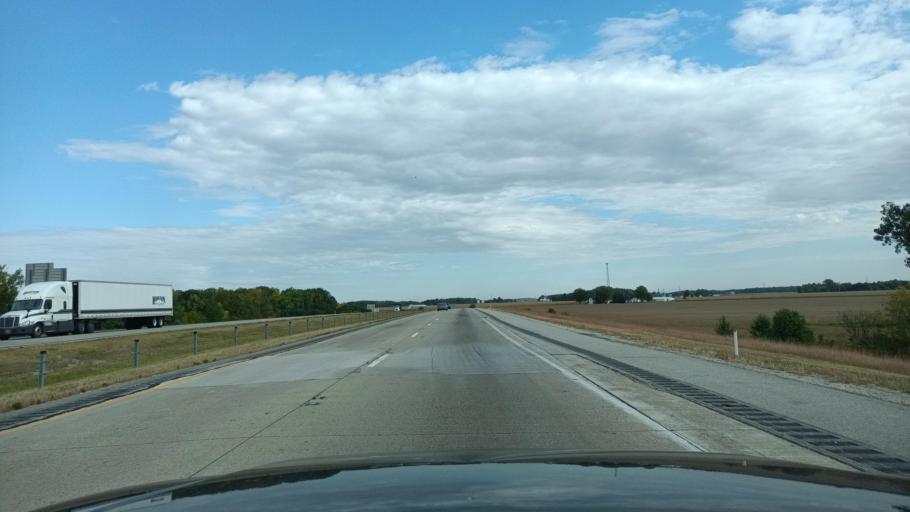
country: US
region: Indiana
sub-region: Huntington County
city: Markle
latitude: 40.8318
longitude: -85.3494
